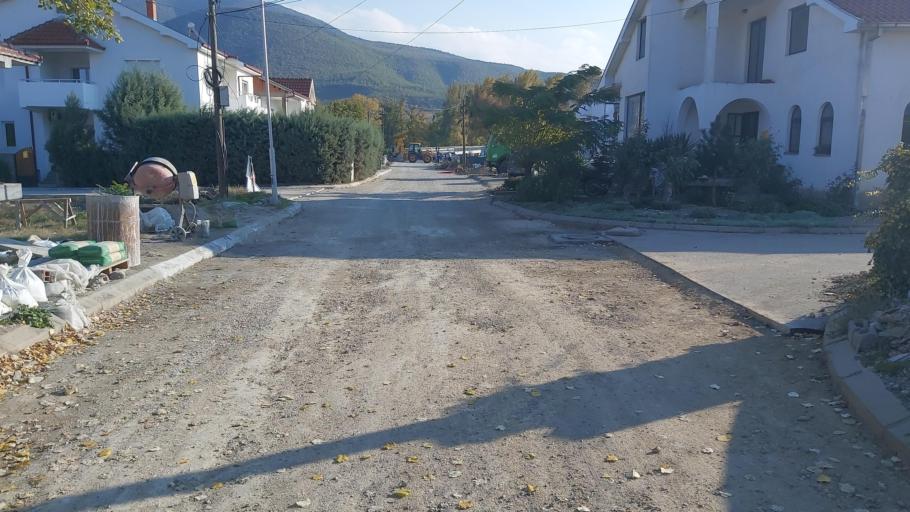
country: MK
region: Demir Kapija
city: Demir Kapija
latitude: 41.4080
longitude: 22.2424
